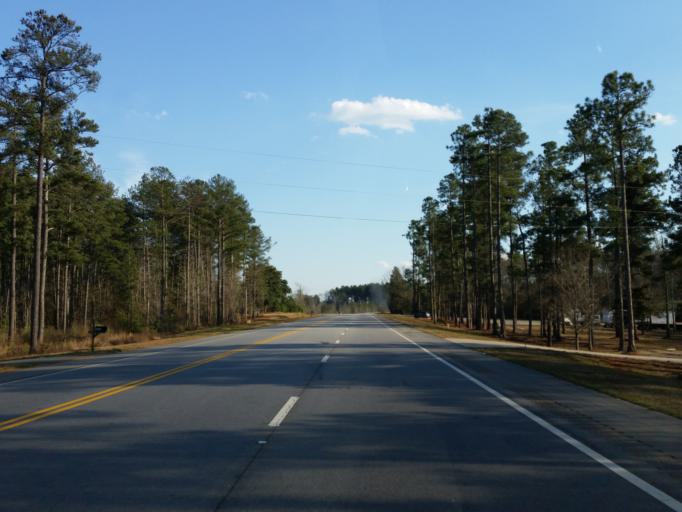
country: US
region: Georgia
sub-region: Monroe County
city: Forsyth
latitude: 33.0405
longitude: -84.0046
